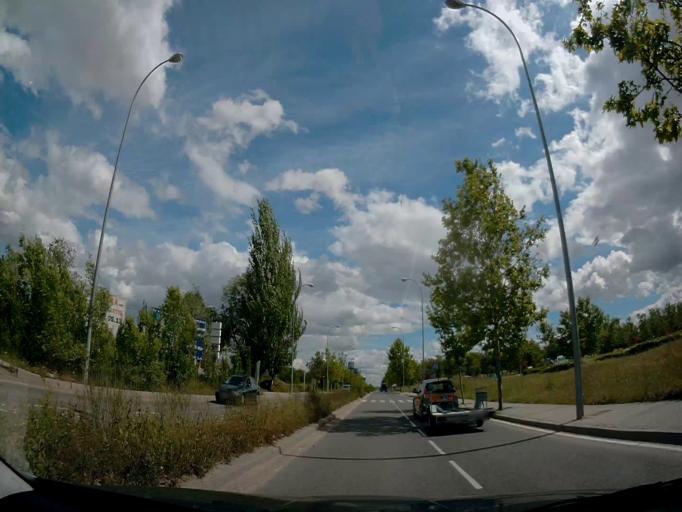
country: ES
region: Madrid
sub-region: Provincia de Madrid
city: Vicalvaro
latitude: 40.4172
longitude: -3.6108
